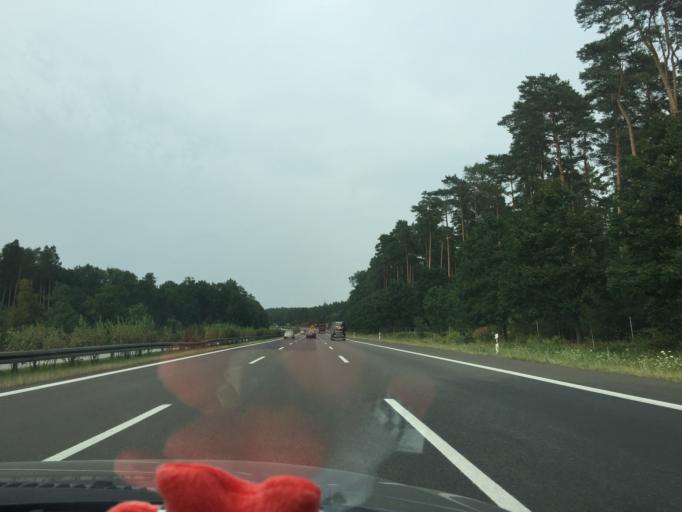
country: DE
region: Brandenburg
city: Grunheide
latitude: 52.4372
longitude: 13.7971
